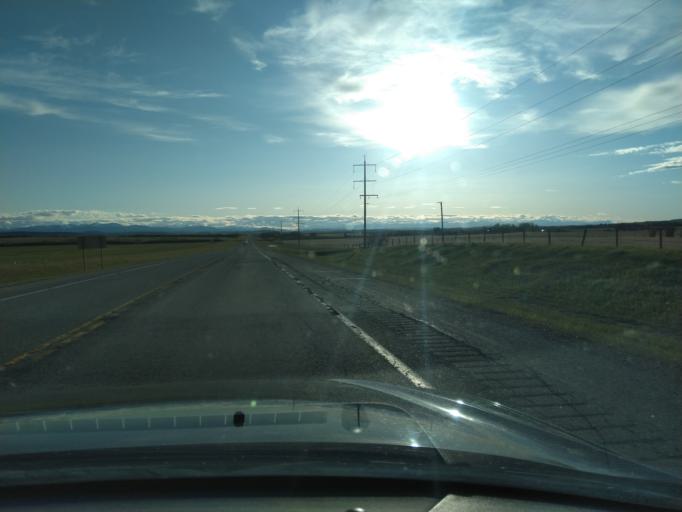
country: CA
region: Alberta
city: Cochrane
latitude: 51.0235
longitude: -114.3392
